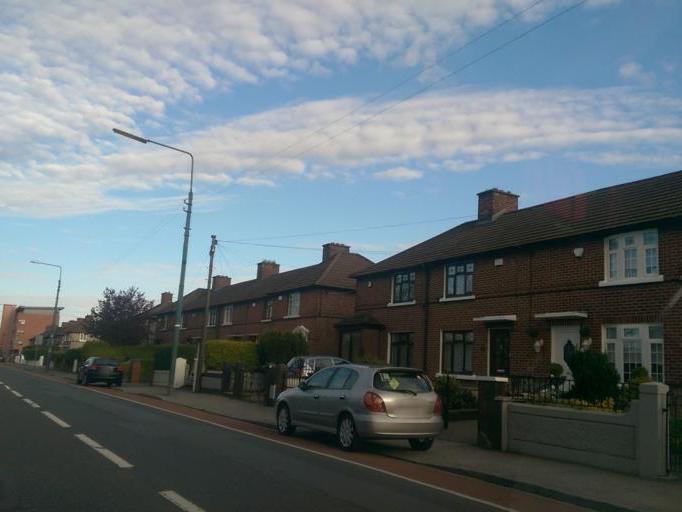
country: IE
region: Leinster
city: Rialto
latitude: 53.3313
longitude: -6.2893
